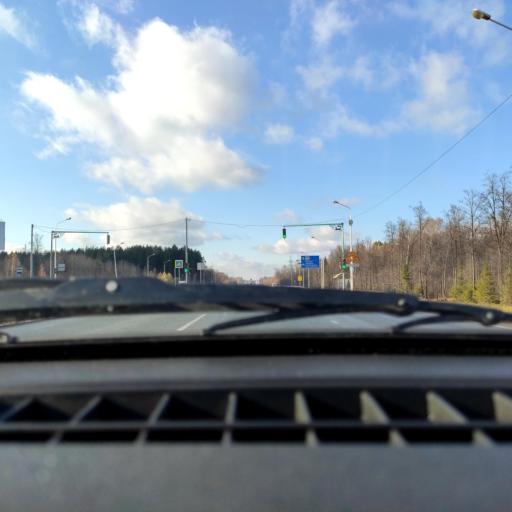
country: RU
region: Bashkortostan
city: Ufa
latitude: 54.6651
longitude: 56.0710
